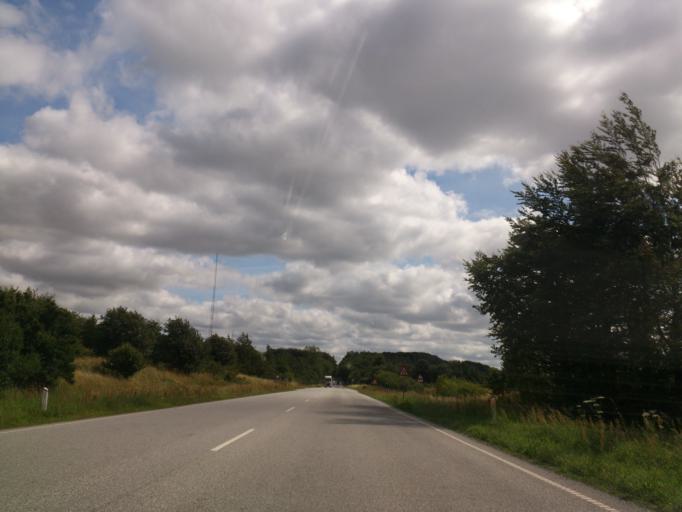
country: DK
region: South Denmark
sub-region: Aabenraa Kommune
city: Aabenraa
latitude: 54.9692
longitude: 9.4480
